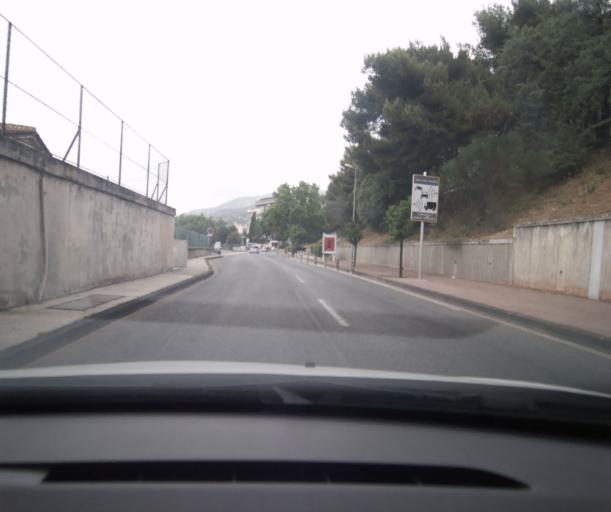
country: FR
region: Provence-Alpes-Cote d'Azur
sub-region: Departement du Var
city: Toulon
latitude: 43.1276
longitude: 5.9349
